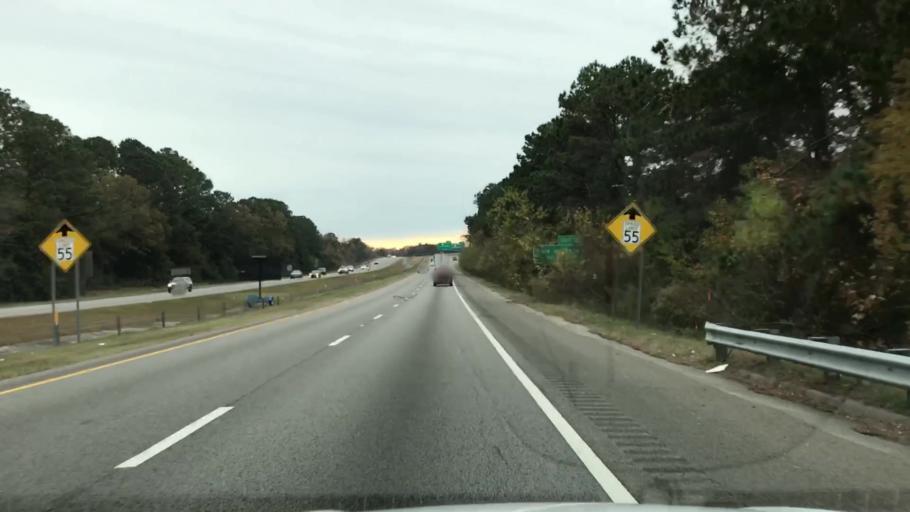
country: US
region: South Carolina
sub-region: Charleston County
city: Mount Pleasant
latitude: 32.8288
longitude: -79.8518
